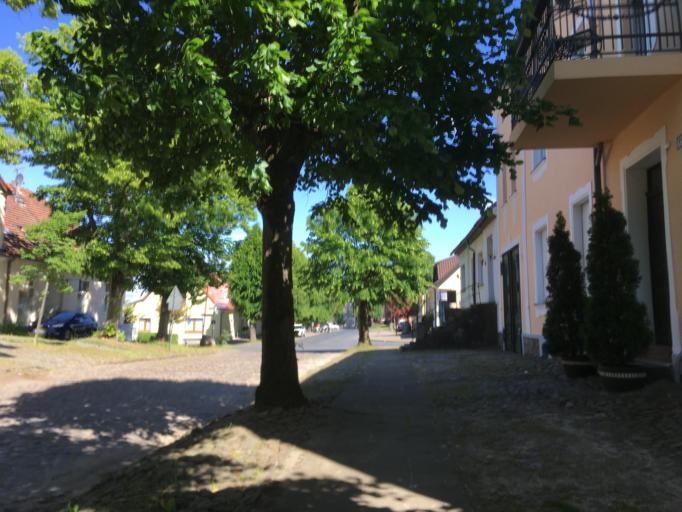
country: DE
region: Brandenburg
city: Joachimsthal
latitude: 52.9767
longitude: 13.7410
